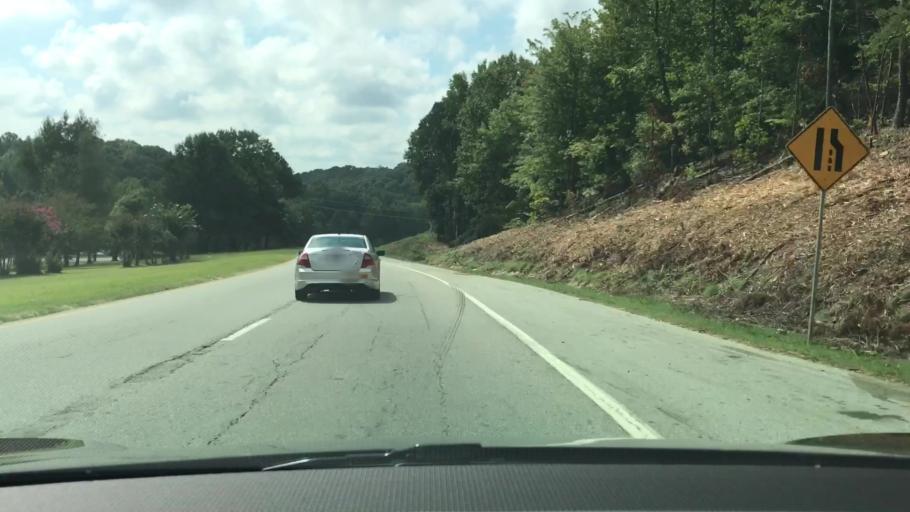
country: US
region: Georgia
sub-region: Hall County
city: Gainesville
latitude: 34.2841
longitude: -83.8089
